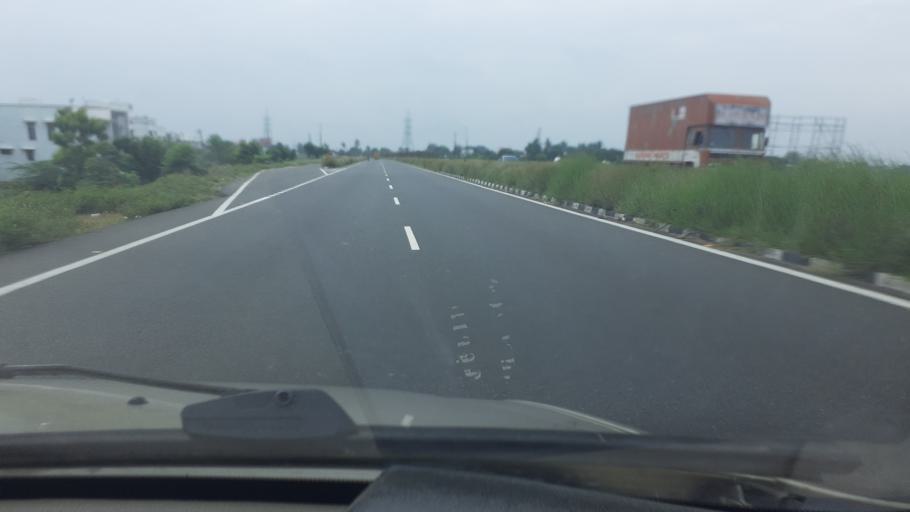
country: IN
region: Tamil Nadu
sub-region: Madurai
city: Tirupparangunram
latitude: 9.8369
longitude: 77.9913
